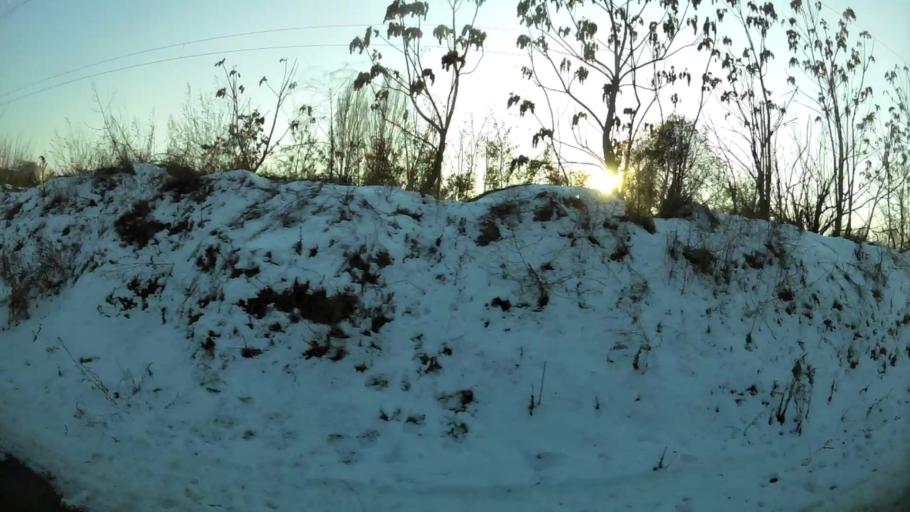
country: MK
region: Kisela Voda
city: Usje
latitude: 41.9731
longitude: 21.4667
